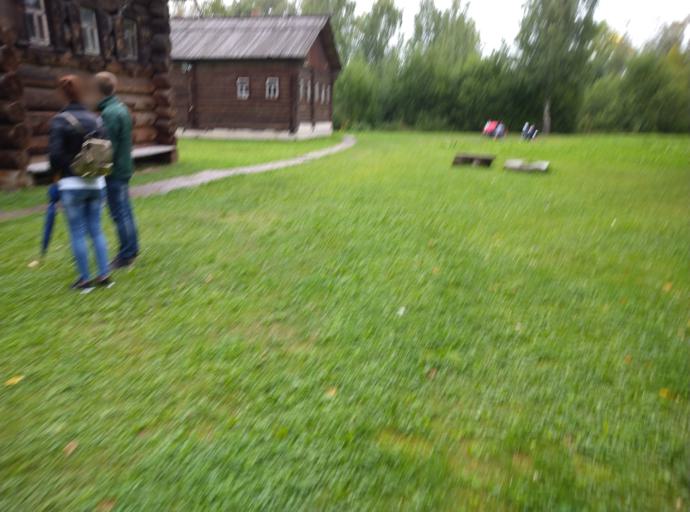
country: RU
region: Kostroma
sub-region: Kostromskoy Rayon
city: Kostroma
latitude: 57.7758
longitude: 40.8902
